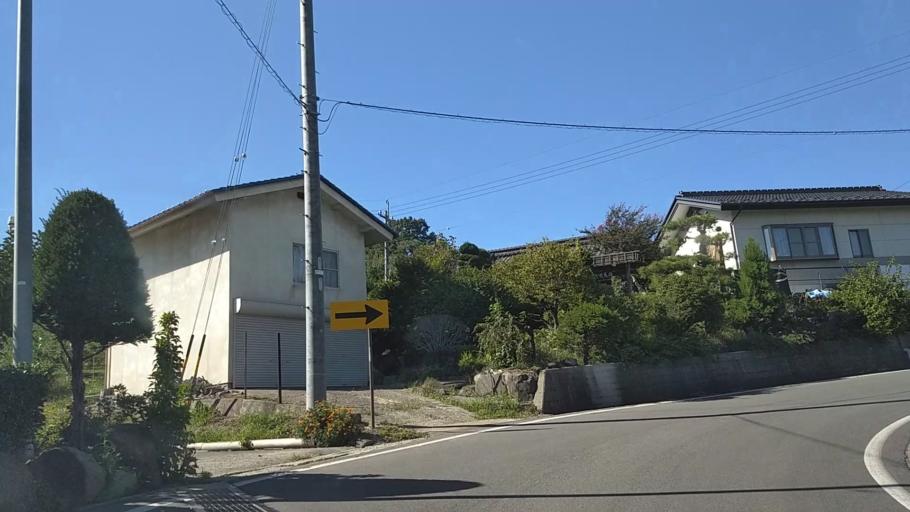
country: JP
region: Nagano
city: Nagano-shi
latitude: 36.5785
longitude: 138.1253
